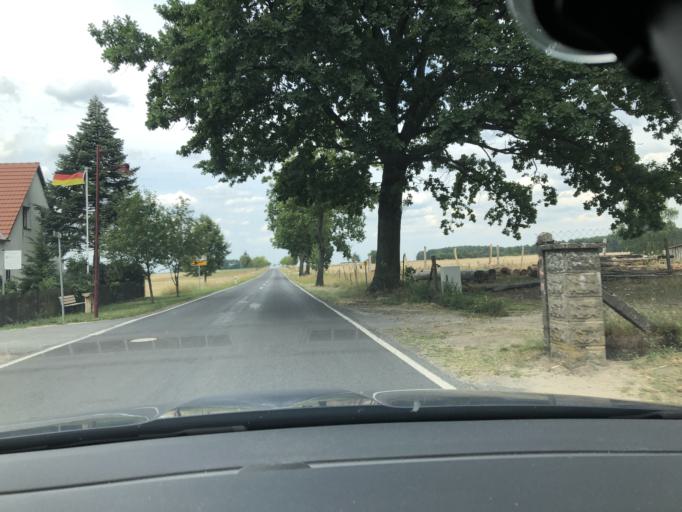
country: DE
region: Brandenburg
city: Munchehofe
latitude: 52.1640
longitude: 13.9207
